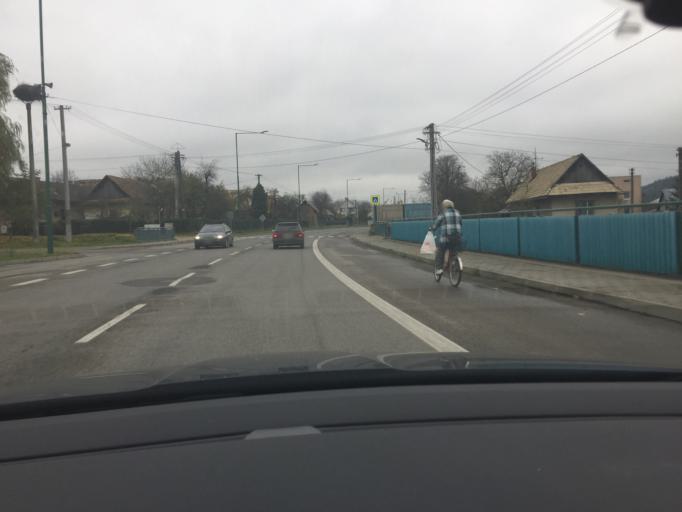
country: SK
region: Presovsky
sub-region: Okres Bardejov
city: Bardejov
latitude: 49.3088
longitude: 21.2121
